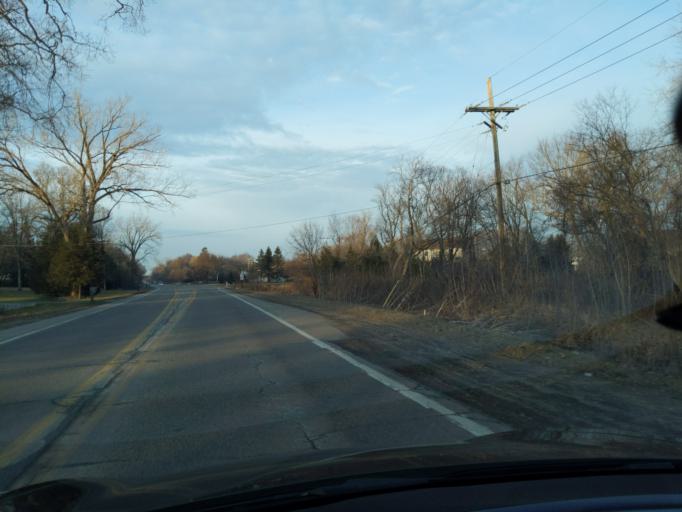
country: US
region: Michigan
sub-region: Livingston County
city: Brighton
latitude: 42.5688
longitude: -83.7529
